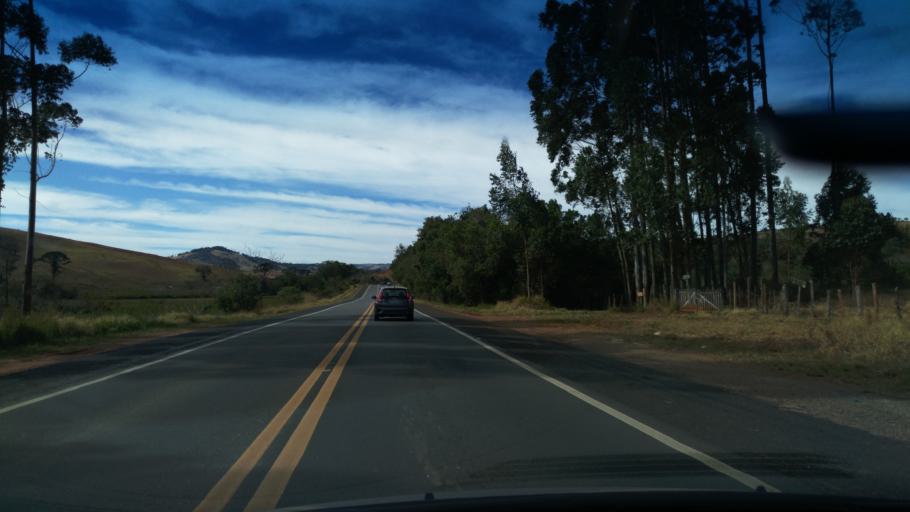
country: BR
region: Minas Gerais
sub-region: Borda Da Mata
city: Borda da Mata
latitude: -22.0747
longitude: -46.2583
